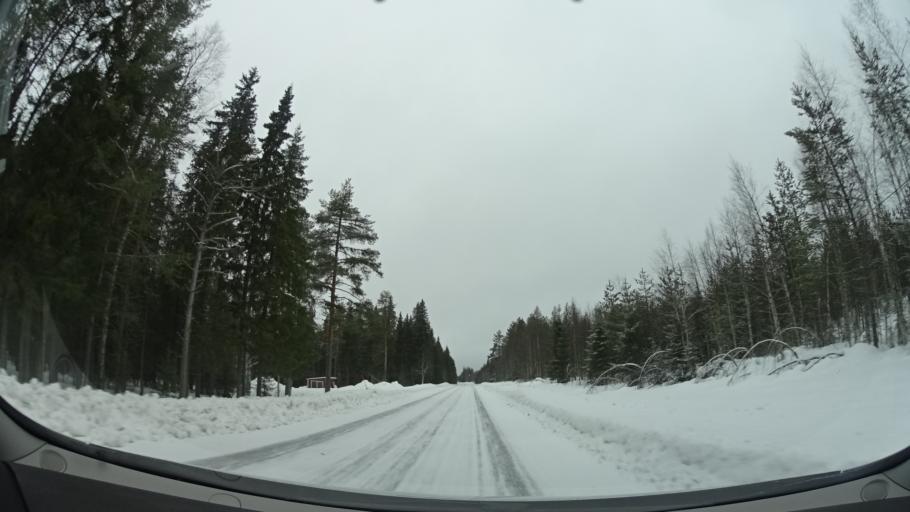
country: SE
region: Vaesterbotten
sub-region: Mala Kommun
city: Mala
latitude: 65.0960
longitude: 18.9262
